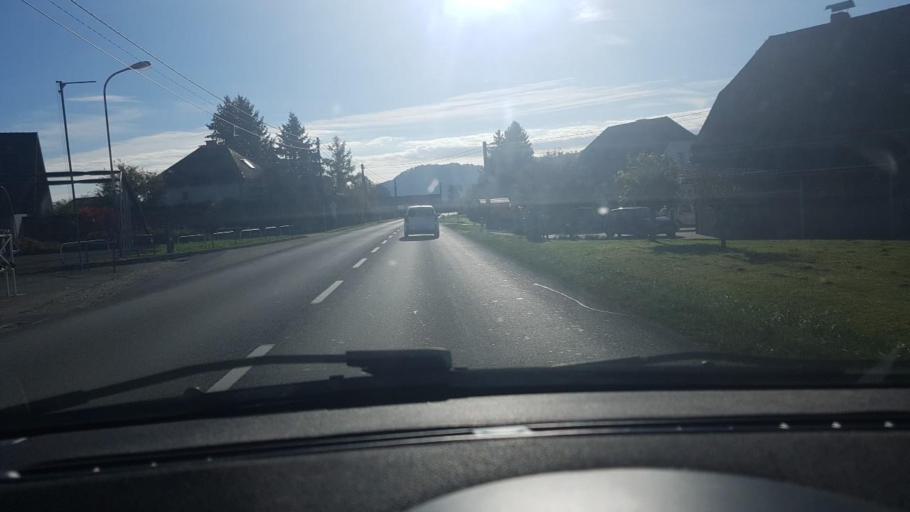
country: AT
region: Styria
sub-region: Politischer Bezirk Leibnitz
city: Weitendorf
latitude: 46.9026
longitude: 15.4844
